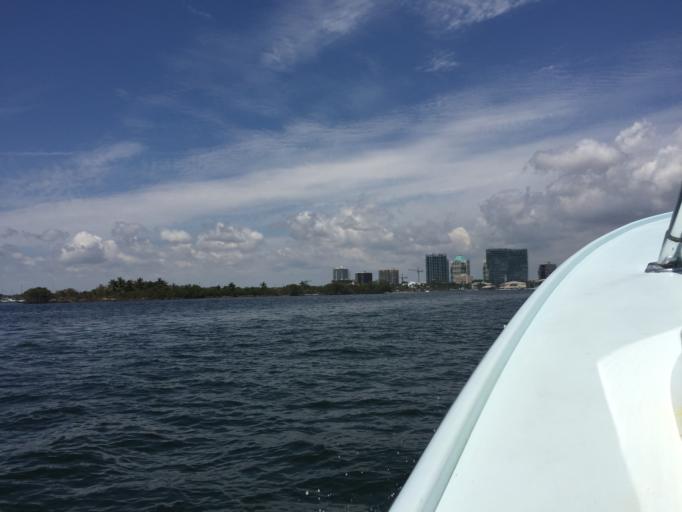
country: US
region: Florida
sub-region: Miami-Dade County
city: Coconut Grove
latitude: 25.7255
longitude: -80.2236
